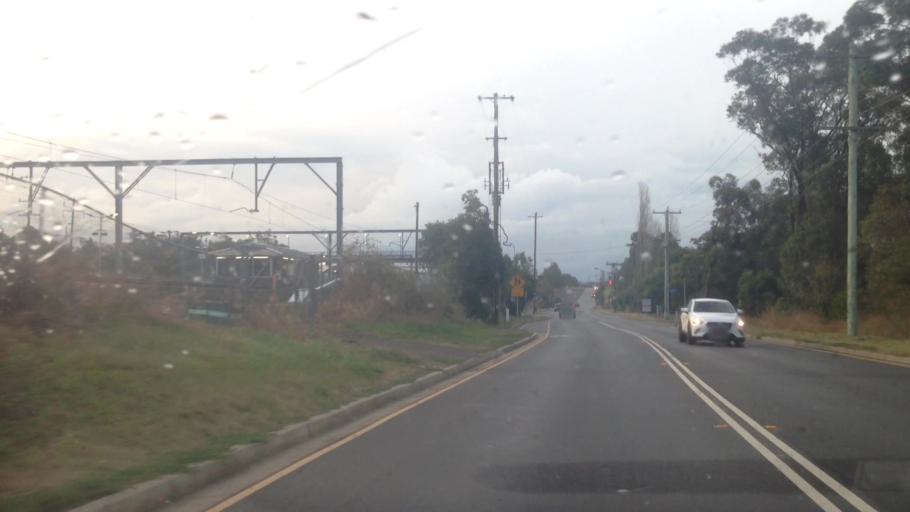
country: AU
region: New South Wales
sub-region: Wyong Shire
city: Charmhaven
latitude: -33.1813
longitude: 151.4874
